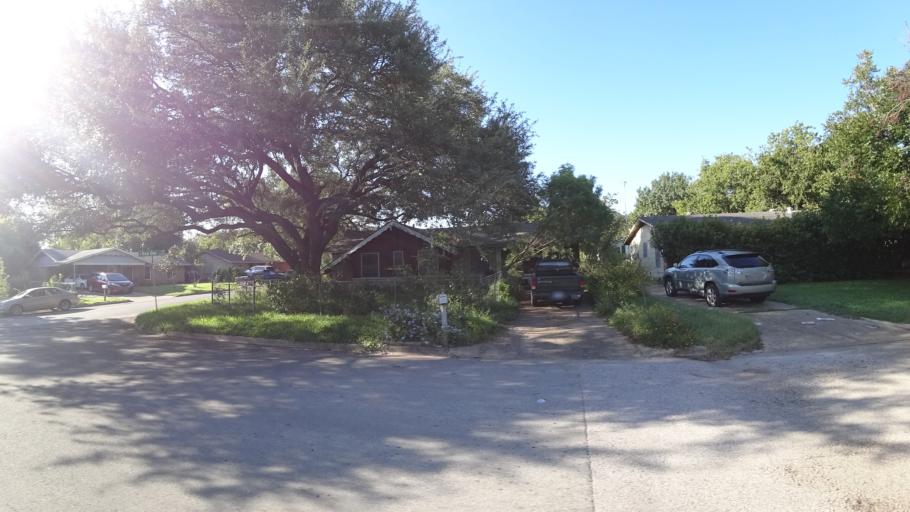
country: US
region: Texas
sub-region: Travis County
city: Austin
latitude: 30.3484
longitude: -97.7007
